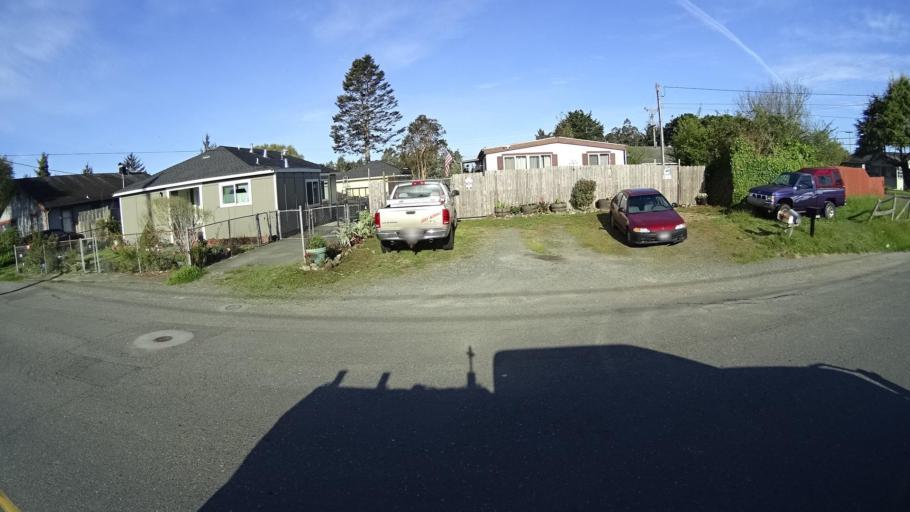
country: US
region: California
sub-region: Humboldt County
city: Bayview
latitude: 40.7667
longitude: -124.1807
